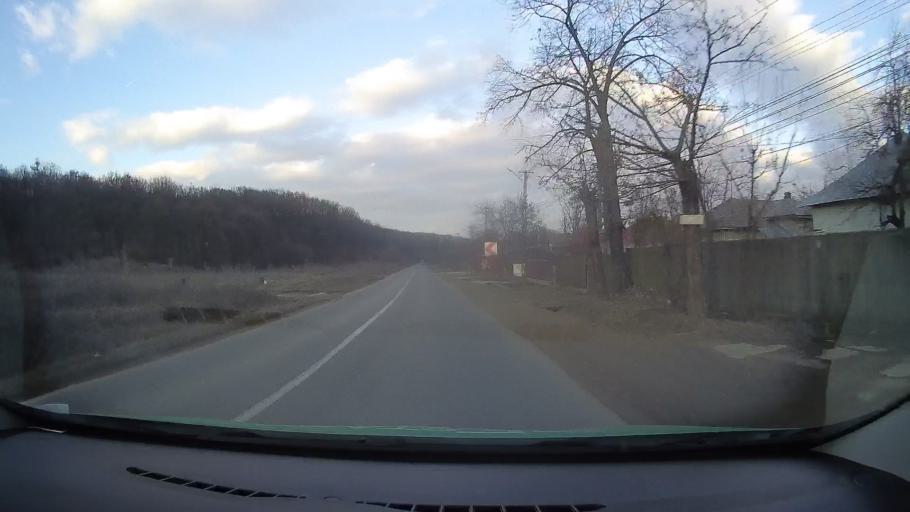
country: RO
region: Dambovita
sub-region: Comuna Gura Ocnitei
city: Gura Ocnitei
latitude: 44.9425
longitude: 25.5827
